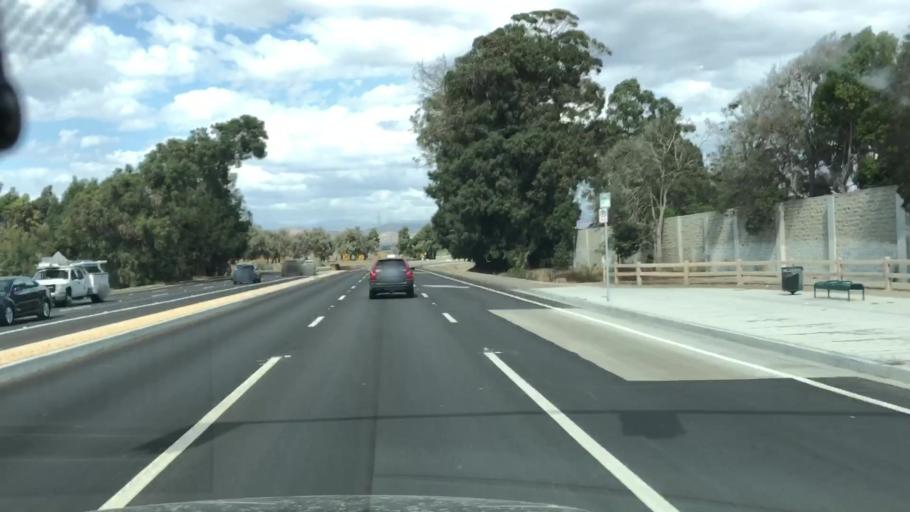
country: US
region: California
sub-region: Ventura County
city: Oxnard Shores
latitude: 34.2252
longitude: -119.2210
